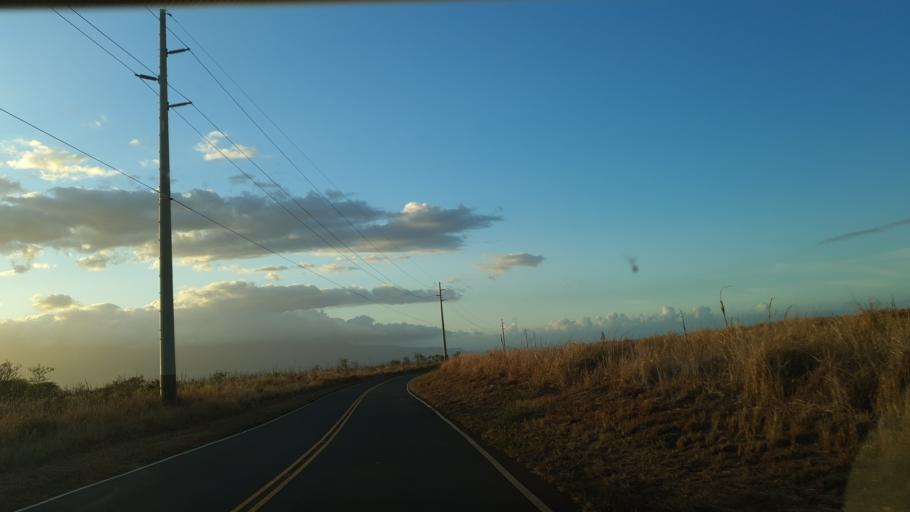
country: US
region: Hawaii
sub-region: Maui County
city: Pukalani
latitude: 20.8037
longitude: -156.3776
